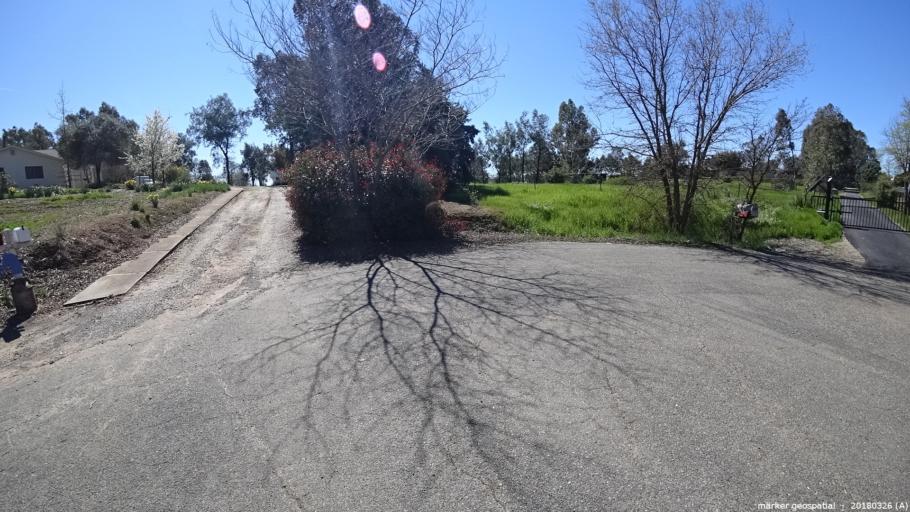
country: US
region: California
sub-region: Sacramento County
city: Wilton
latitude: 38.4758
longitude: -121.2282
